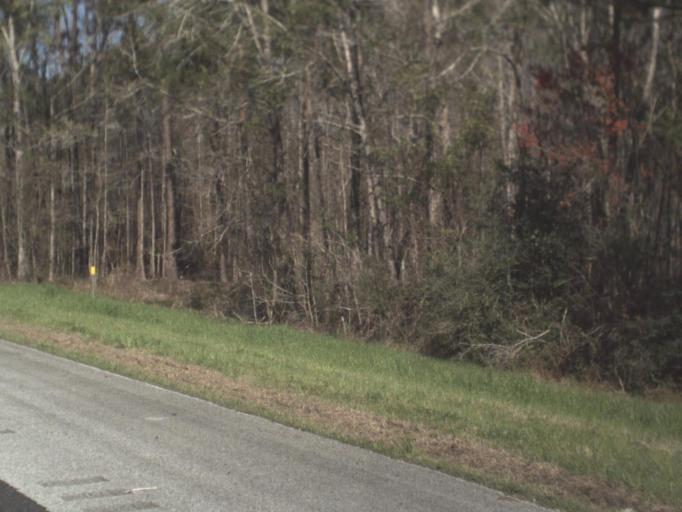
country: US
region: Florida
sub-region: Jackson County
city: Marianna
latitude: 30.6810
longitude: -85.0912
